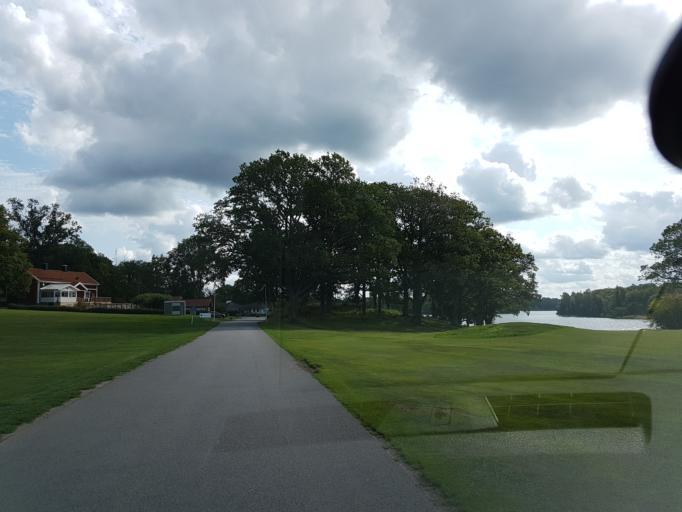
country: SE
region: OEstergoetland
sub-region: Atvidabergs Kommun
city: Atvidaberg
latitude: 58.1949
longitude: 15.9818
